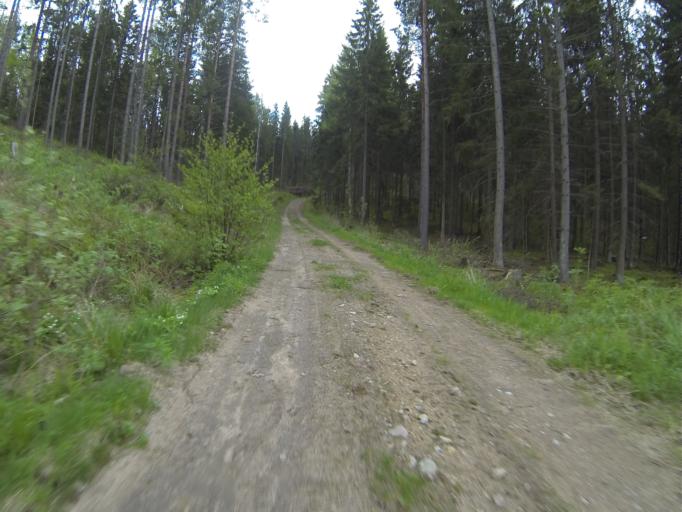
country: FI
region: Varsinais-Suomi
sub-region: Salo
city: Halikko
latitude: 60.3381
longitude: 23.0823
